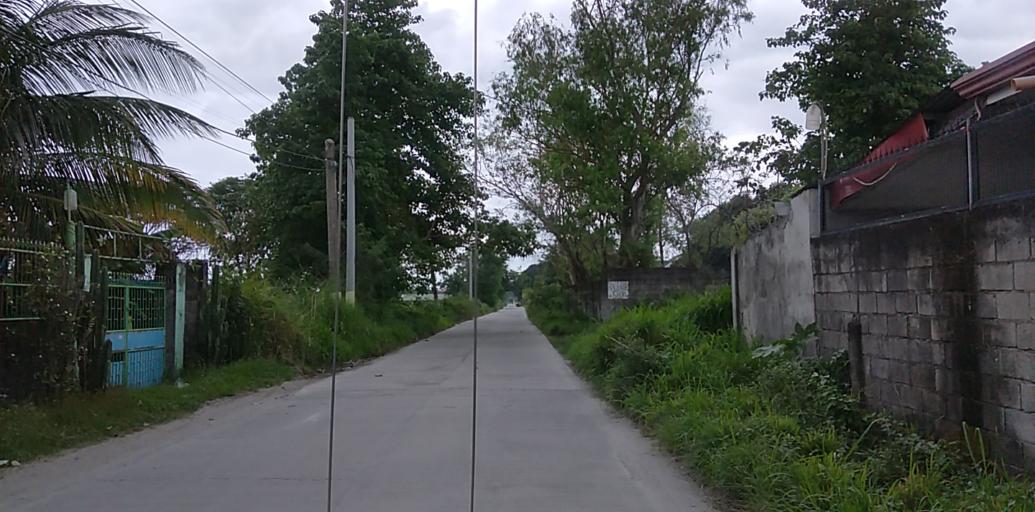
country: PH
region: Central Luzon
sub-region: Province of Pampanga
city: Porac
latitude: 15.0625
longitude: 120.5512
